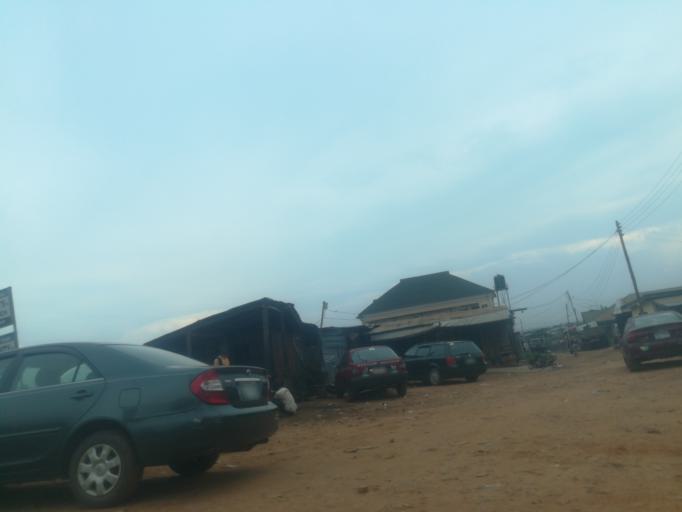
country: NG
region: Oyo
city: Ibadan
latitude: 7.3656
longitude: 3.8151
